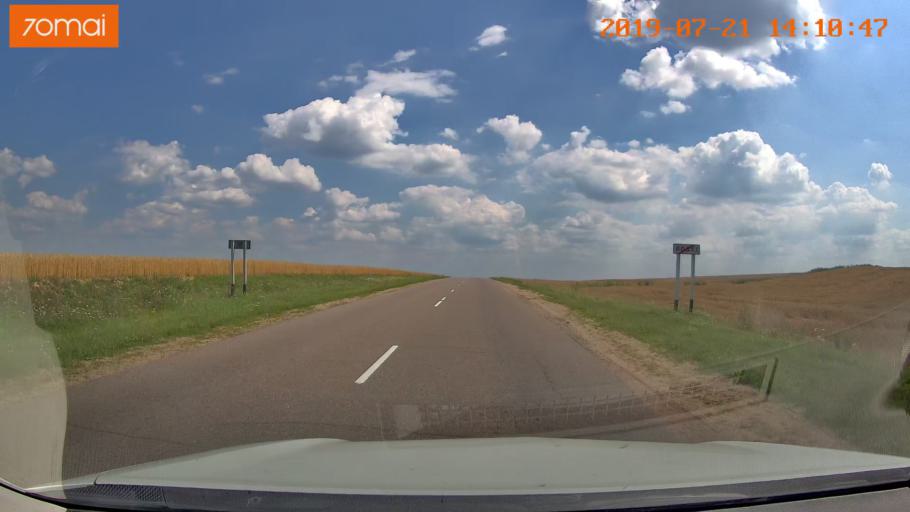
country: BY
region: Grodnenskaya
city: Karelichy
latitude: 53.6620
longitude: 26.1390
